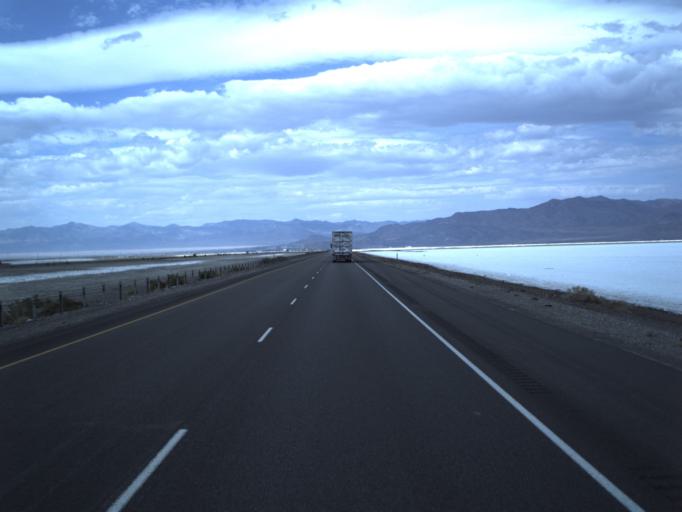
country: US
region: Utah
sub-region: Tooele County
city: Wendover
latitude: 40.7403
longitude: -113.8978
